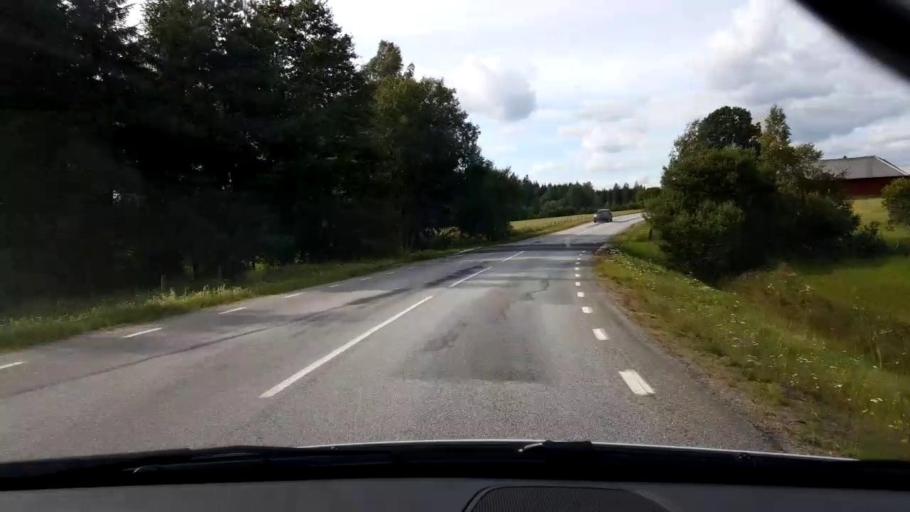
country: SE
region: Joenkoeping
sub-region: Vetlanda Kommun
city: Vetlanda
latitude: 57.3781
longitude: 15.0195
